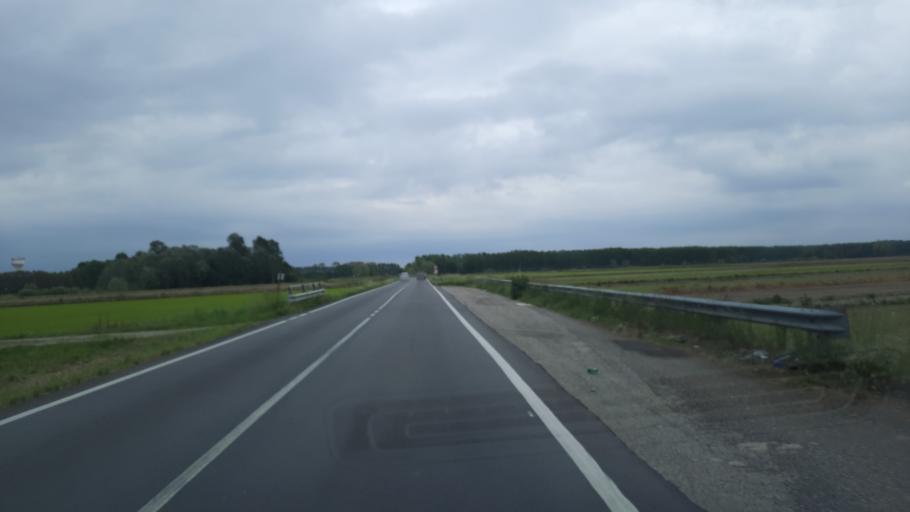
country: IT
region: Lombardy
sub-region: Provincia di Pavia
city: Robbio
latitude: 45.2905
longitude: 8.5672
